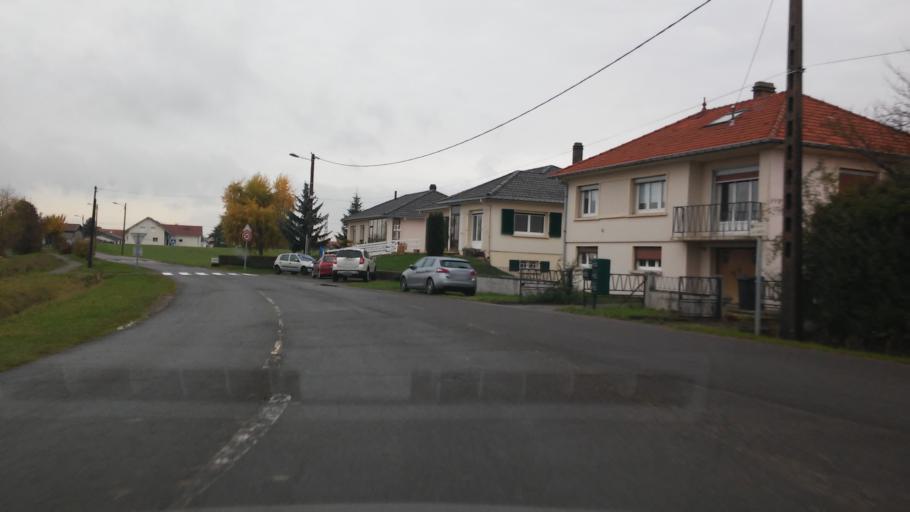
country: FR
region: Lorraine
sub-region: Departement de la Moselle
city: Vigy
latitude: 49.1861
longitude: 6.3324
